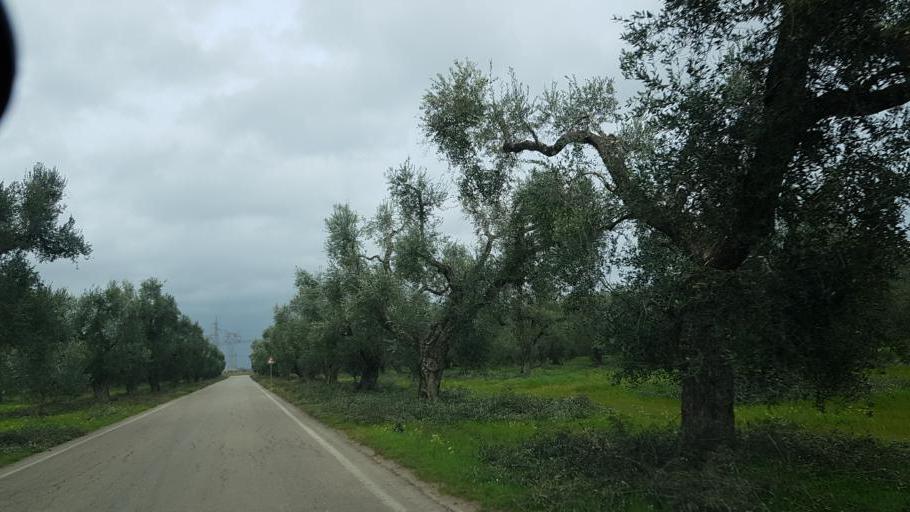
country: IT
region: Apulia
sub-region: Provincia di Brindisi
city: Brindisi
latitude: 40.5971
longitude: 17.8993
